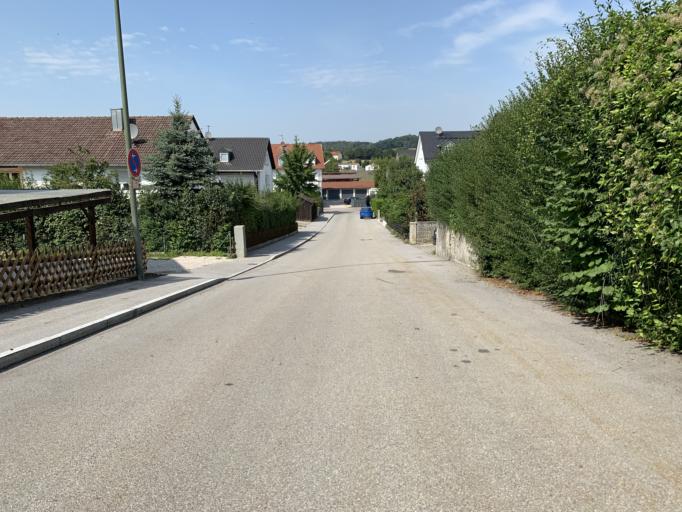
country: DE
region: Bavaria
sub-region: Upper Bavaria
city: Marzling
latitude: 48.4085
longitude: 11.8024
